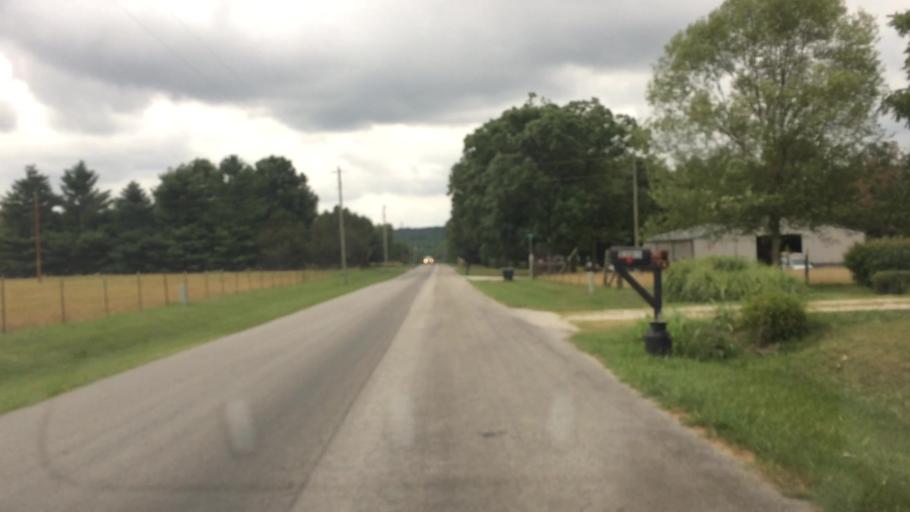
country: US
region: Missouri
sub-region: Webster County
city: Marshfield
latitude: 37.3103
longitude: -92.9845
